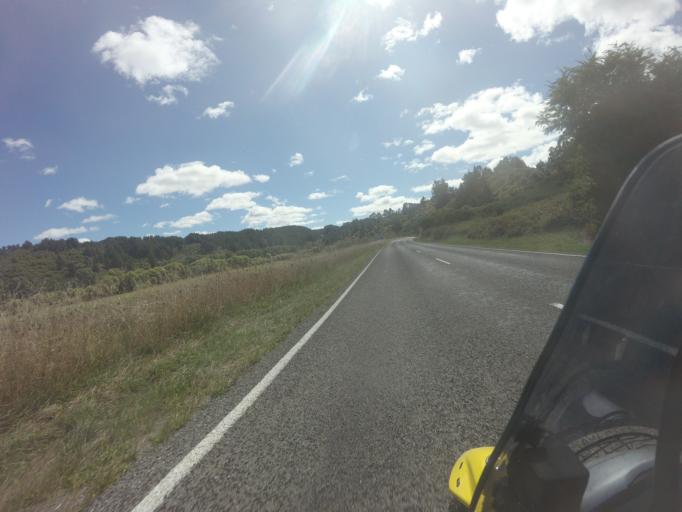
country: NZ
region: Bay of Plenty
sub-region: Kawerau District
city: Kawerau
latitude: -38.1838
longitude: 176.8359
